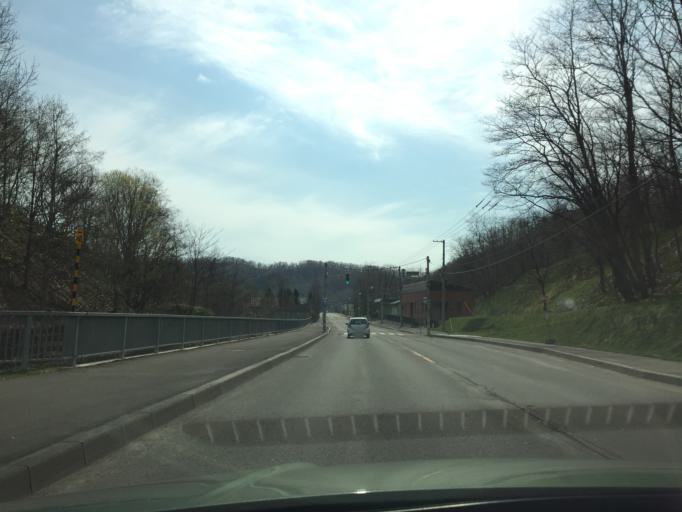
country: JP
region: Hokkaido
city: Utashinai
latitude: 43.5240
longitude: 142.0556
